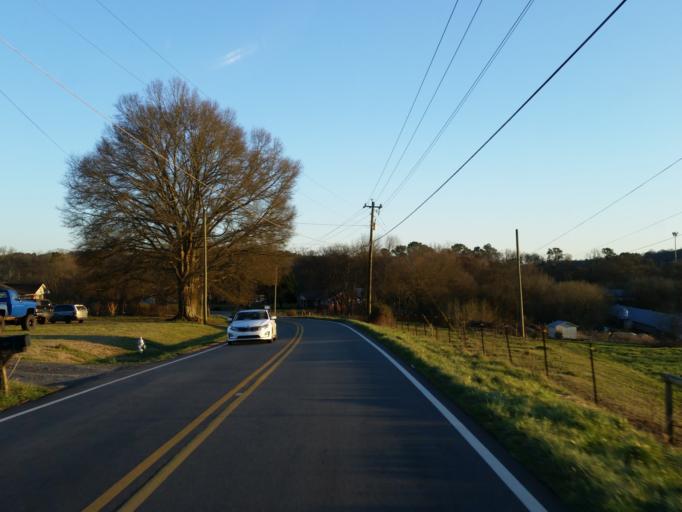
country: US
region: Georgia
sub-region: Cherokee County
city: Holly Springs
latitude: 34.1435
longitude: -84.4335
